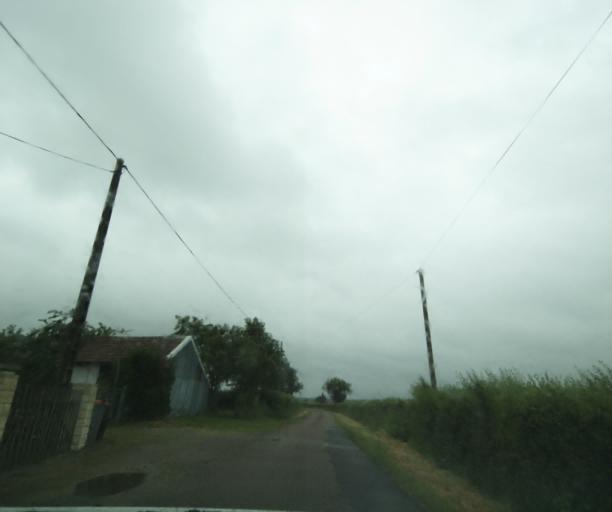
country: FR
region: Bourgogne
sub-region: Departement de Saone-et-Loire
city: Palinges
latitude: 46.4965
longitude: 4.1940
